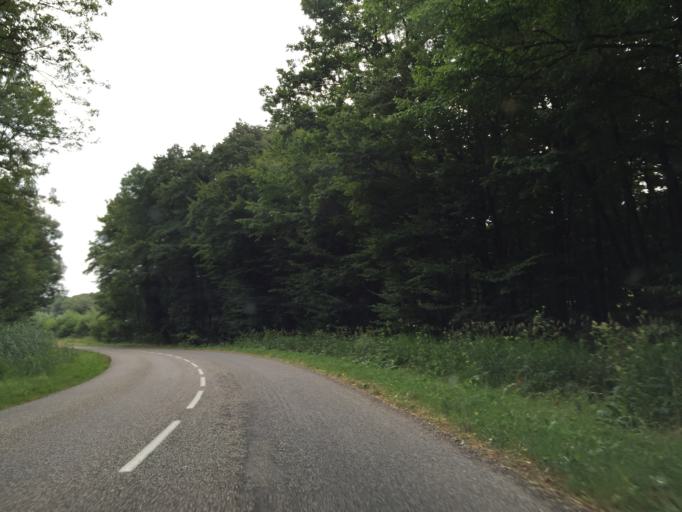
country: FR
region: Alsace
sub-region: Departement du Bas-Rhin
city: Soultz-sous-Forets
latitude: 48.9947
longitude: 7.8730
